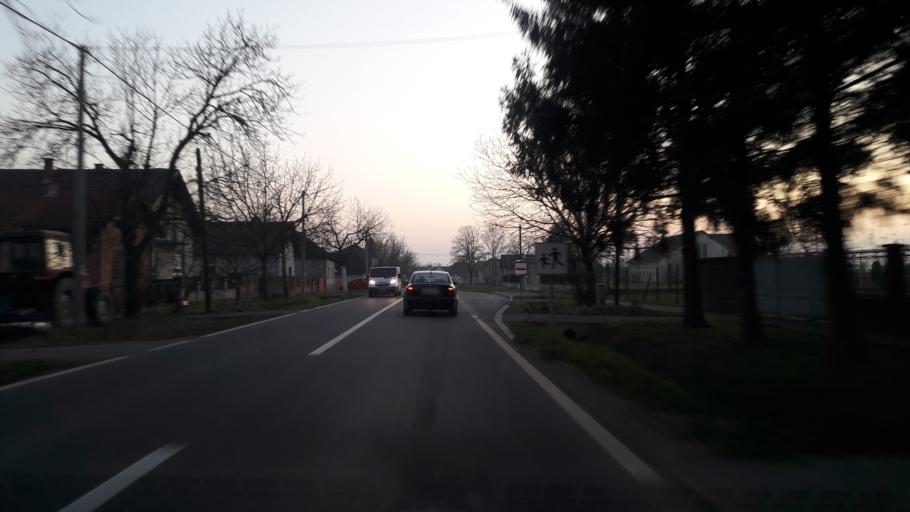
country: HR
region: Vukovarsko-Srijemska
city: Slakovci
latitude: 45.2219
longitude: 18.9882
